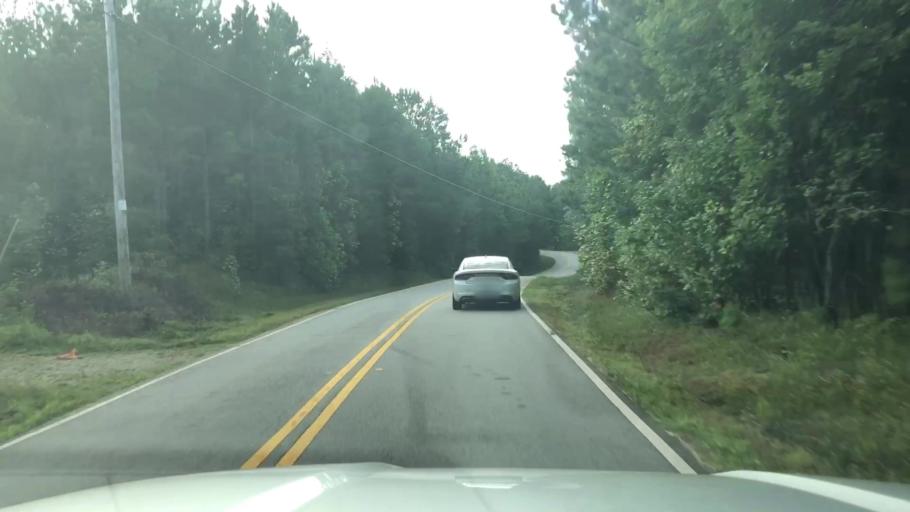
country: US
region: Georgia
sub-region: Paulding County
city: Dallas
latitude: 34.0455
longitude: -84.8585
